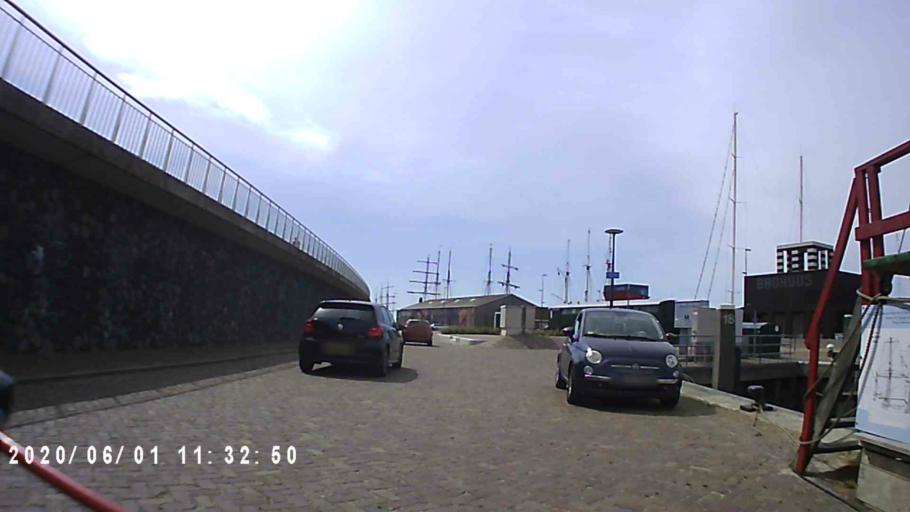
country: NL
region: Friesland
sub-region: Gemeente Harlingen
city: Harlingen
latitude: 53.1737
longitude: 5.4110
